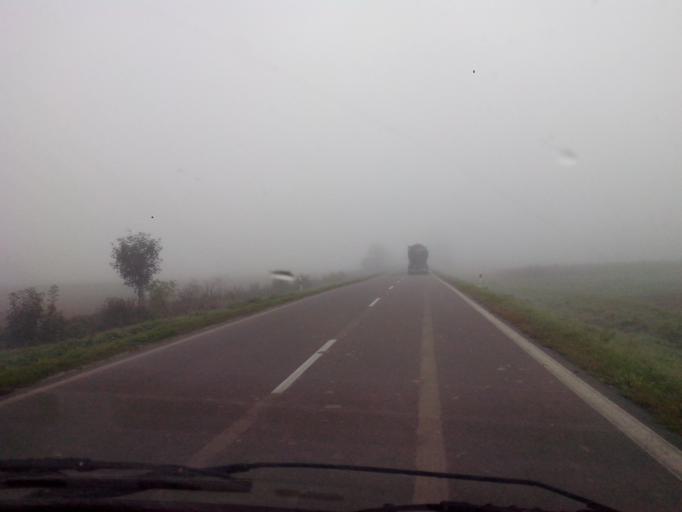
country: PL
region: Subcarpathian Voivodeship
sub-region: Powiat przemyski
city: Krasiczyn
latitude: 49.7982
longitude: 22.6409
